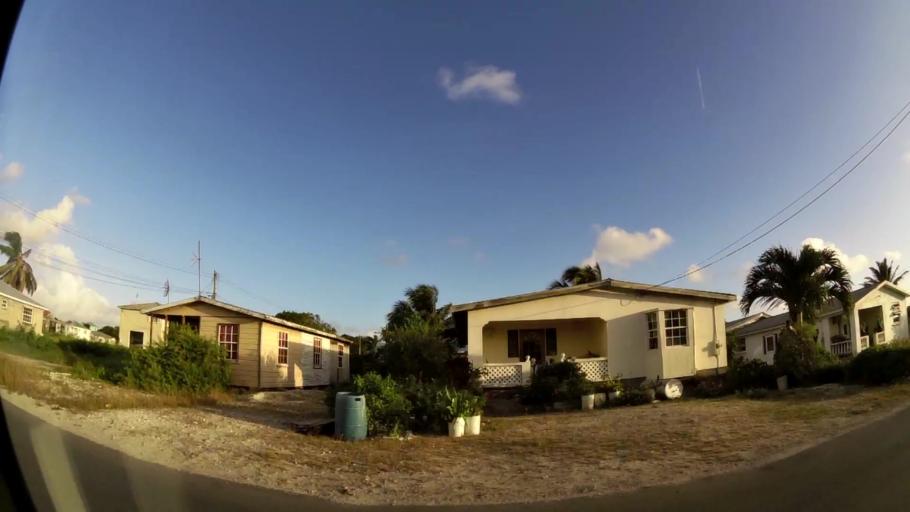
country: BB
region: Christ Church
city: Oistins
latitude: 13.0806
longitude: -59.4972
